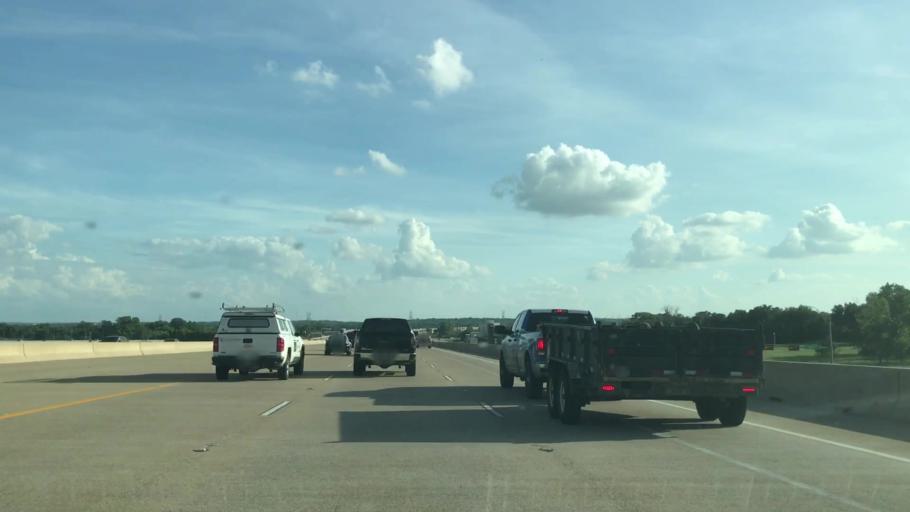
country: US
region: Texas
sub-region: Dallas County
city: Grand Prairie
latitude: 32.8000
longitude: -97.0188
